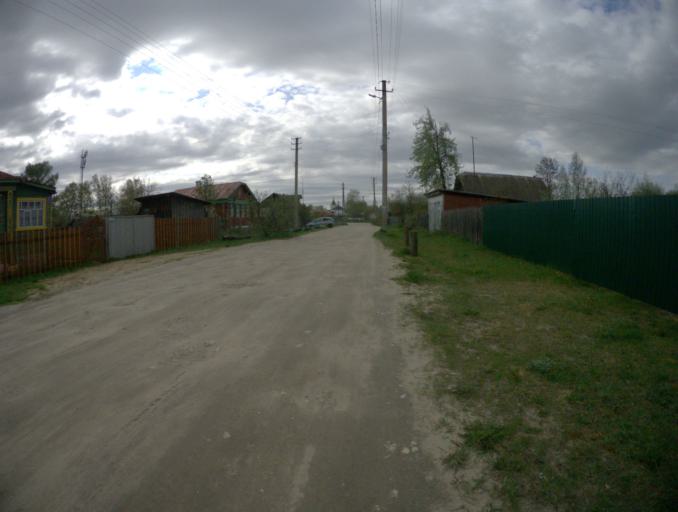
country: RU
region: Vladimir
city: Golovino
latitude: 55.9476
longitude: 40.4486
